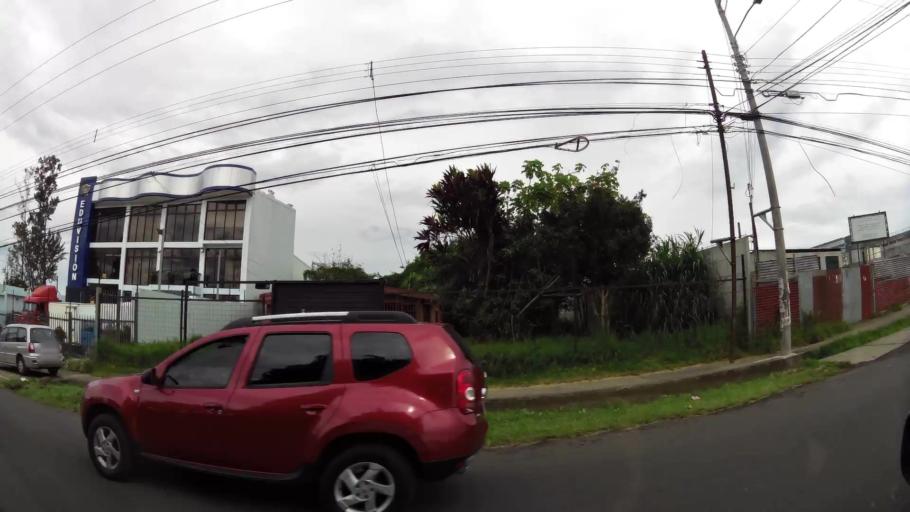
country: CR
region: San Jose
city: Ipis
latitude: 9.9713
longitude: -84.0137
